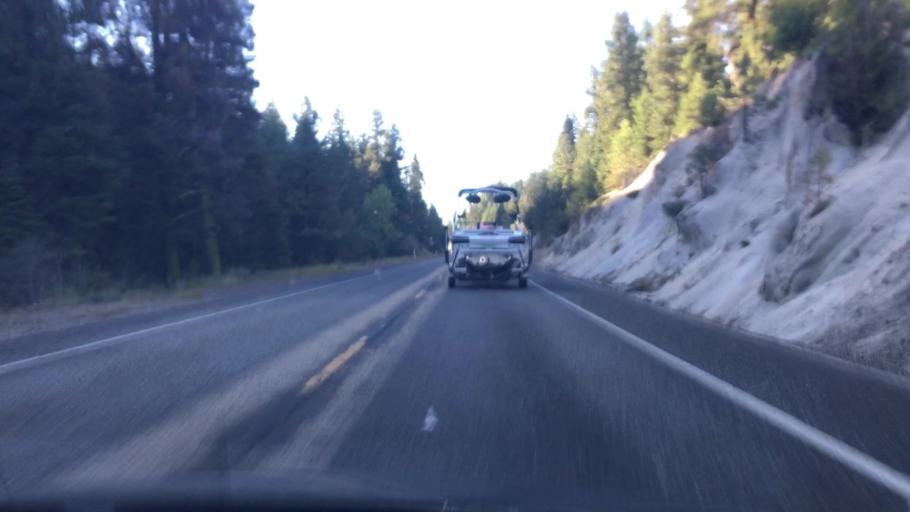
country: US
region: Idaho
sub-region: Valley County
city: Cascade
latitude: 44.5744
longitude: -116.0329
